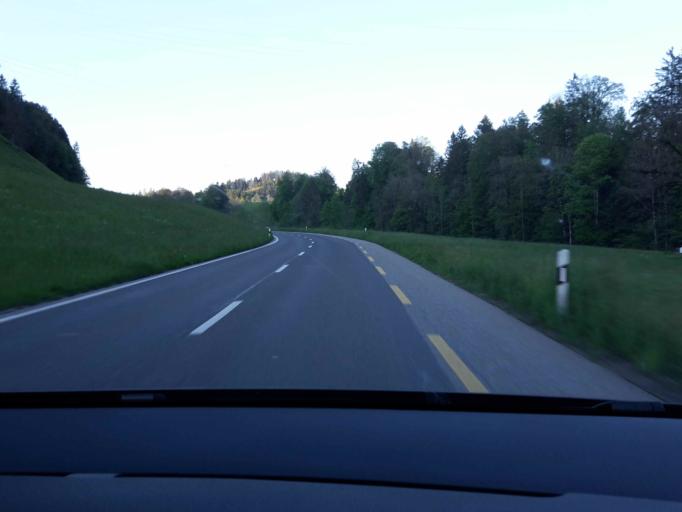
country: CH
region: Bern
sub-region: Emmental District
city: Lutzelfluh
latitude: 47.0291
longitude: 7.6830
